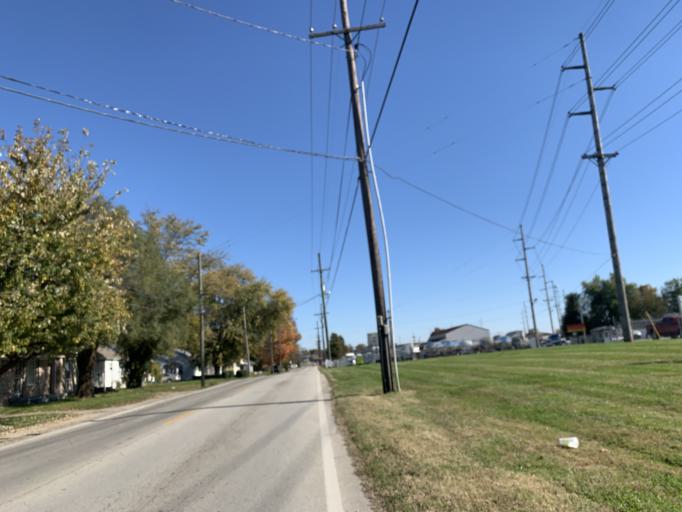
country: US
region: Kentucky
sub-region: Jefferson County
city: Shively
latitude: 38.2216
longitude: -85.8165
